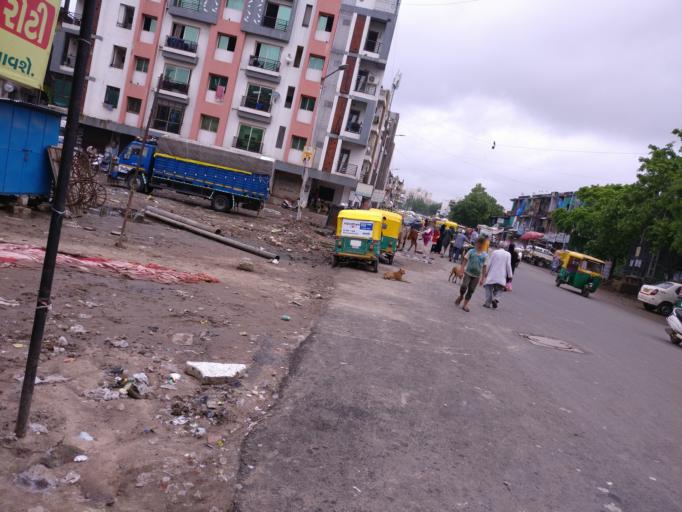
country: IN
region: Gujarat
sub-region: Ahmadabad
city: Sarkhej
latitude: 22.9932
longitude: 72.5192
